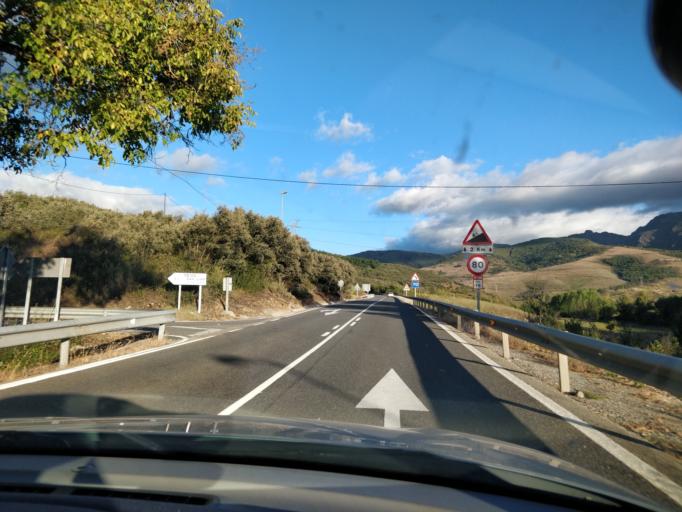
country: ES
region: Castille and Leon
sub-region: Provincia de Leon
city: Borrenes
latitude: 42.4991
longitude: -6.7257
